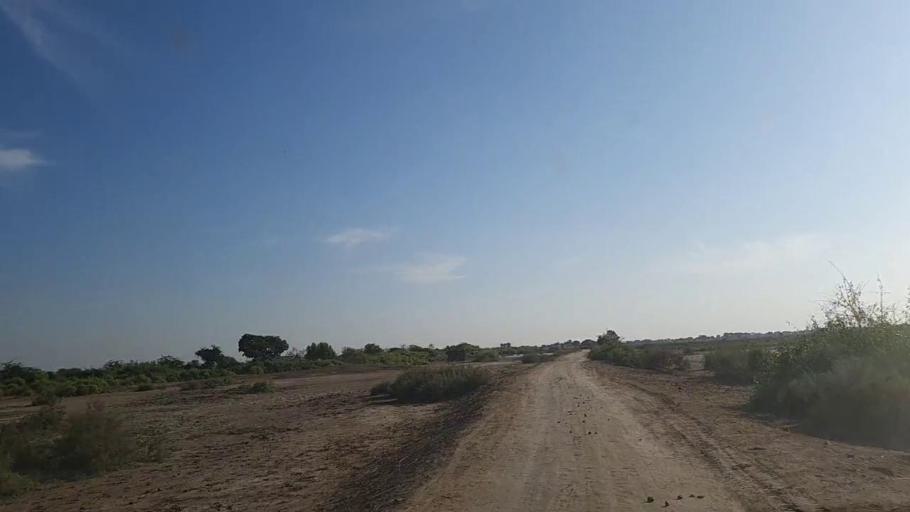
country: PK
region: Sindh
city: Mirpur Batoro
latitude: 24.7599
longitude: 68.3644
